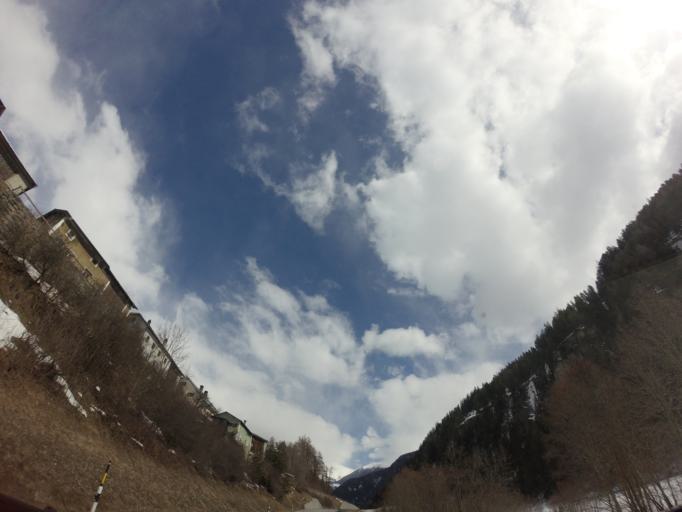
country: AT
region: Tyrol
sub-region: Politischer Bezirk Landeck
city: Nauders
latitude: 46.8627
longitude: 10.4363
